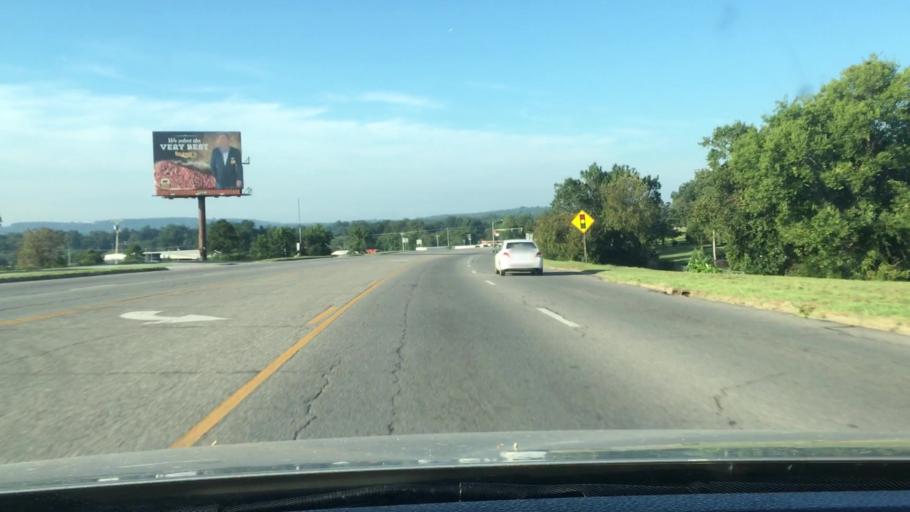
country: US
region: Oklahoma
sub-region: Cherokee County
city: Park Hill
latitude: 35.8606
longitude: -94.9777
